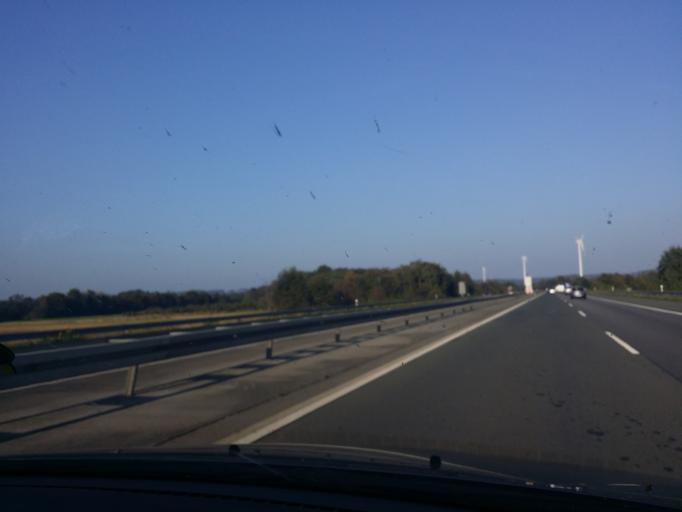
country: DE
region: North Rhine-Westphalia
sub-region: Regierungsbezirk Munster
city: Ladbergen
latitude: 52.1754
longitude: 7.7722
